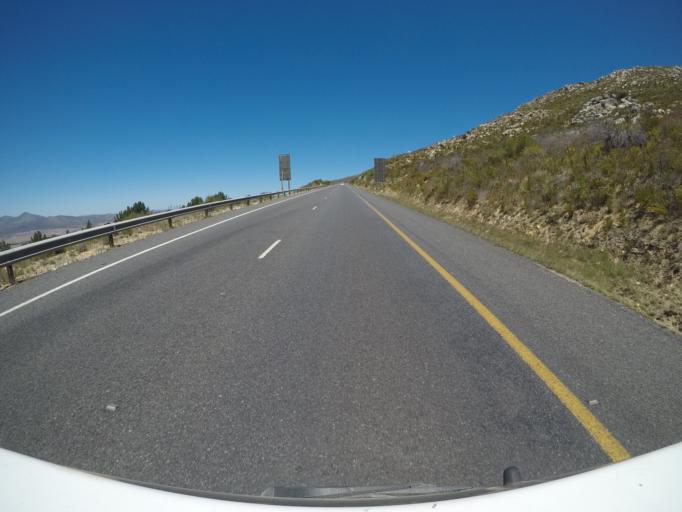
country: ZA
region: Western Cape
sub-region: Overberg District Municipality
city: Grabouw
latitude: -34.2188
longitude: 19.1859
